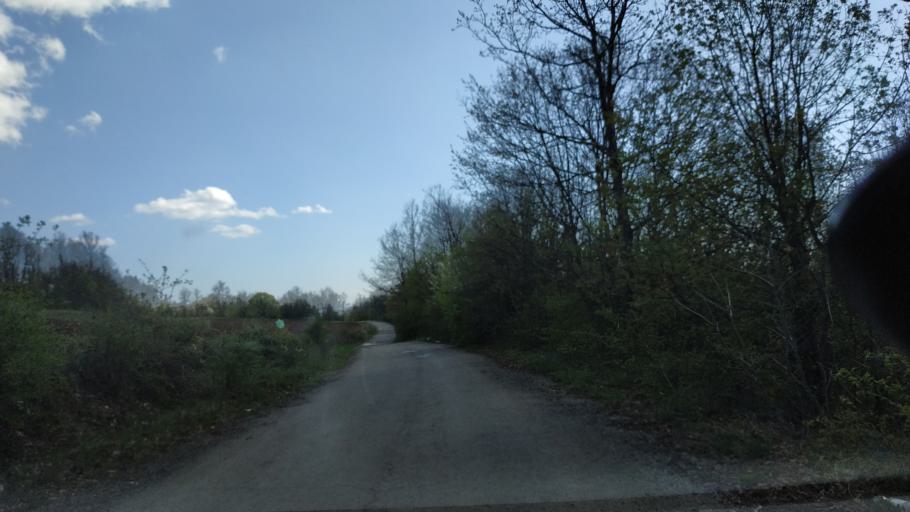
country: RS
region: Central Serbia
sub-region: Zajecarski Okrug
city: Soko Banja
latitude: 43.5578
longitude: 21.8929
